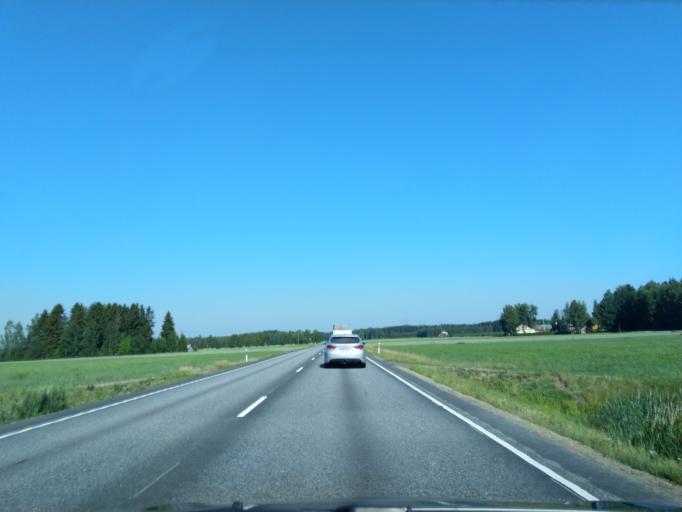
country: FI
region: Varsinais-Suomi
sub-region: Loimaa
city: Alastaro
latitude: 61.0918
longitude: 22.8798
